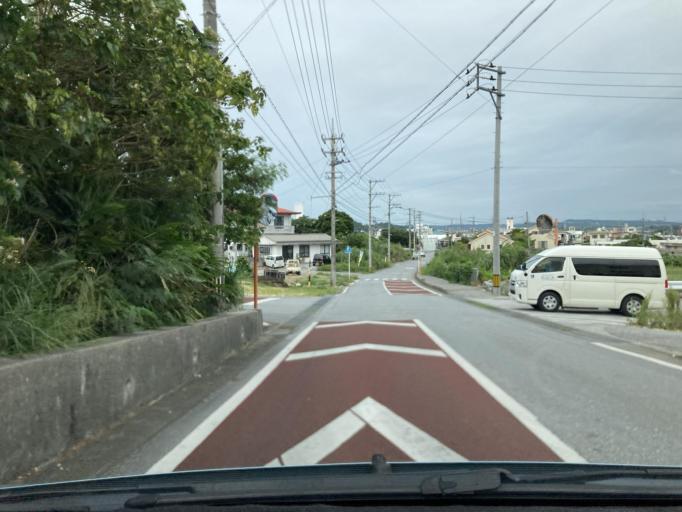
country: JP
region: Okinawa
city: Itoman
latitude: 26.1430
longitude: 127.6834
